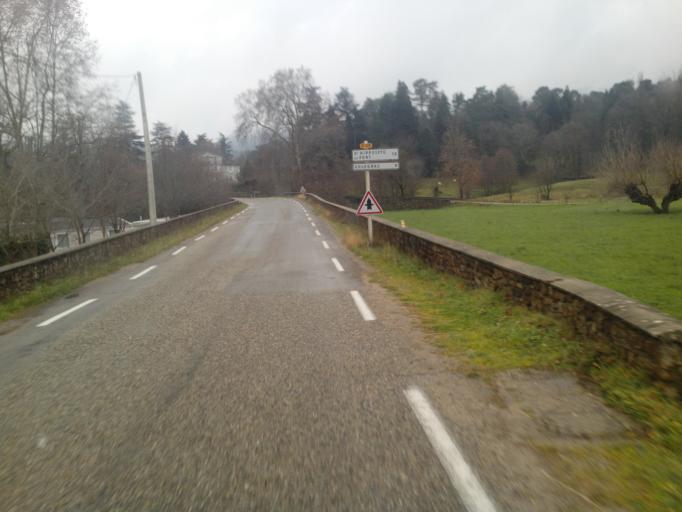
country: FR
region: Languedoc-Roussillon
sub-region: Departement du Gard
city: Lasalle
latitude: 44.0386
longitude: 3.8615
